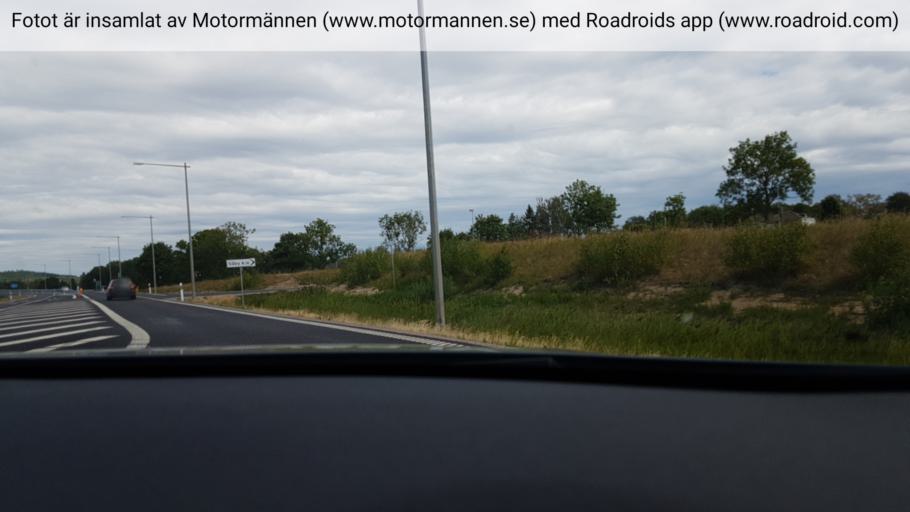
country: SE
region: Joenkoeping
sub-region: Tranas Kommun
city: Tranas
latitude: 57.9915
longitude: 14.9184
